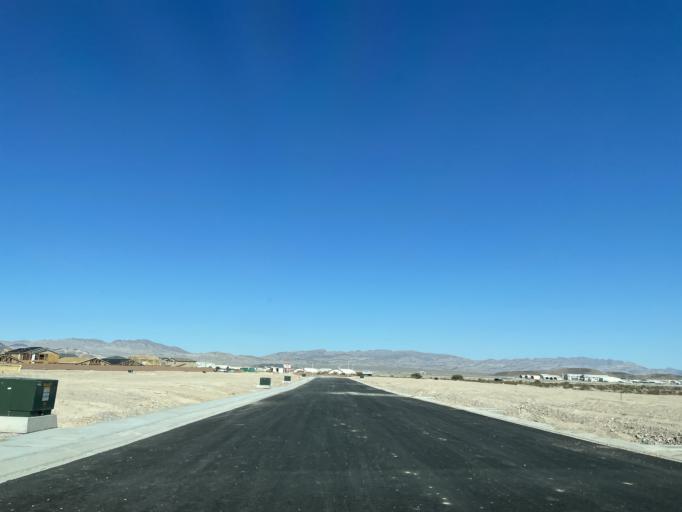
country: US
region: Nevada
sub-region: Nye County
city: Pahrump
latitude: 36.5743
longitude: -115.6617
